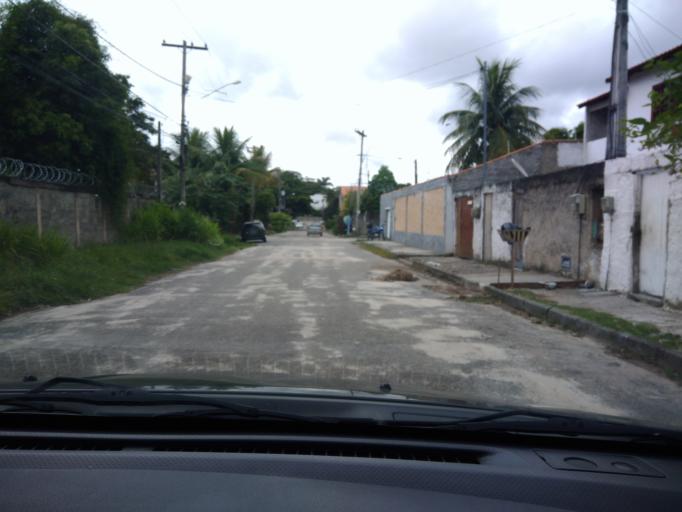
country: BR
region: Rio de Janeiro
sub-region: Niteroi
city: Niteroi
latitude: -22.9304
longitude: -43.0093
